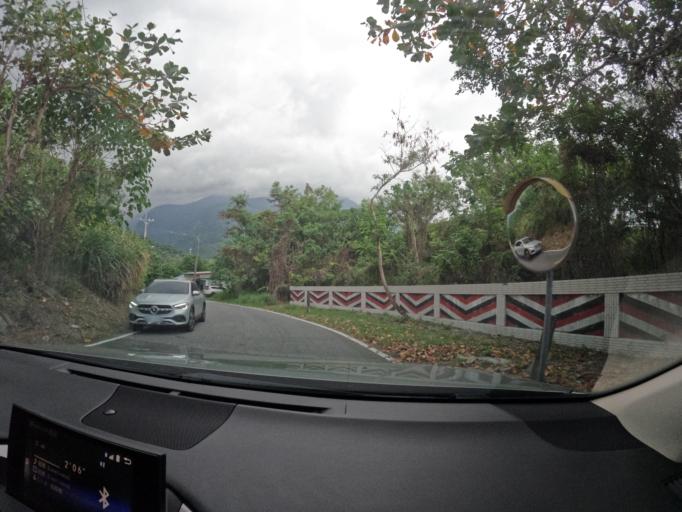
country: TW
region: Taiwan
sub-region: Hualien
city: Hualian
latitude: 24.0926
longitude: 121.6183
